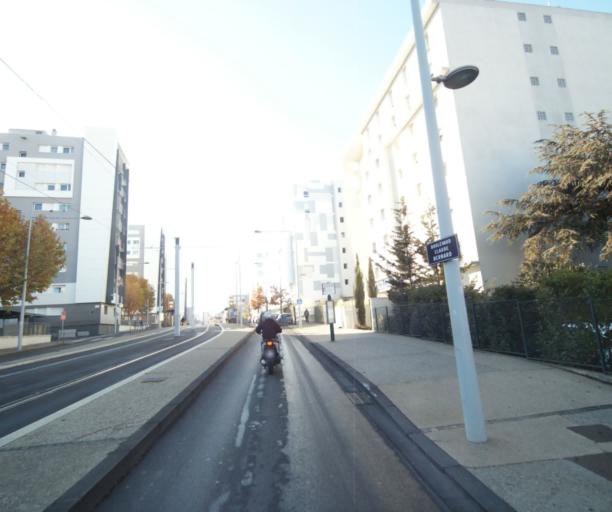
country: FR
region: Auvergne
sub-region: Departement du Puy-de-Dome
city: Clermont-Ferrand
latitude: 45.7655
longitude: 3.0890
